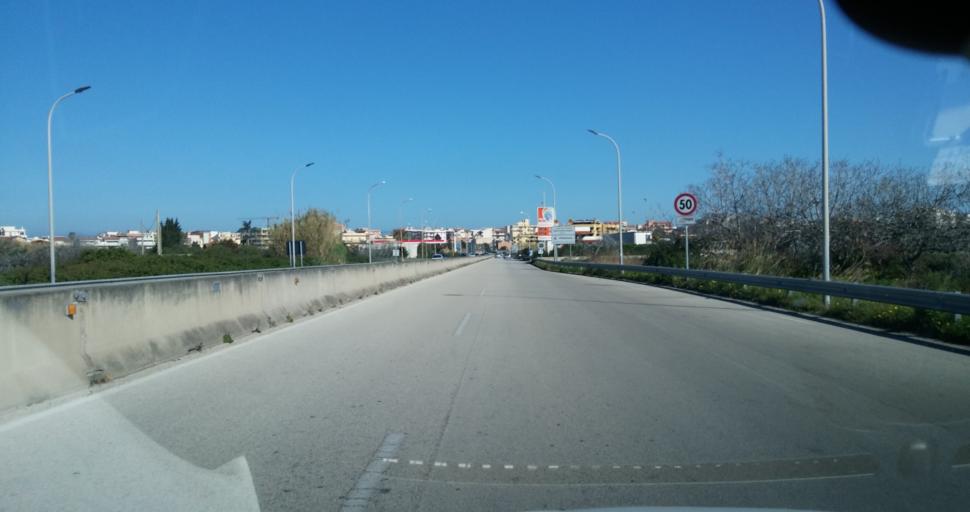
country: IT
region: Sicily
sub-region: Messina
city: Milazzo
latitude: 38.2095
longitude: 15.2377
